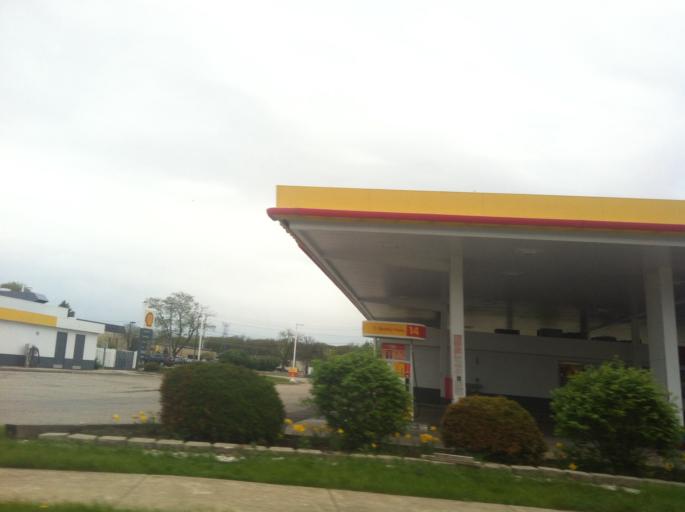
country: US
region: Illinois
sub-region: DuPage County
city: Downers Grove
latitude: 41.8066
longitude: -88.0394
